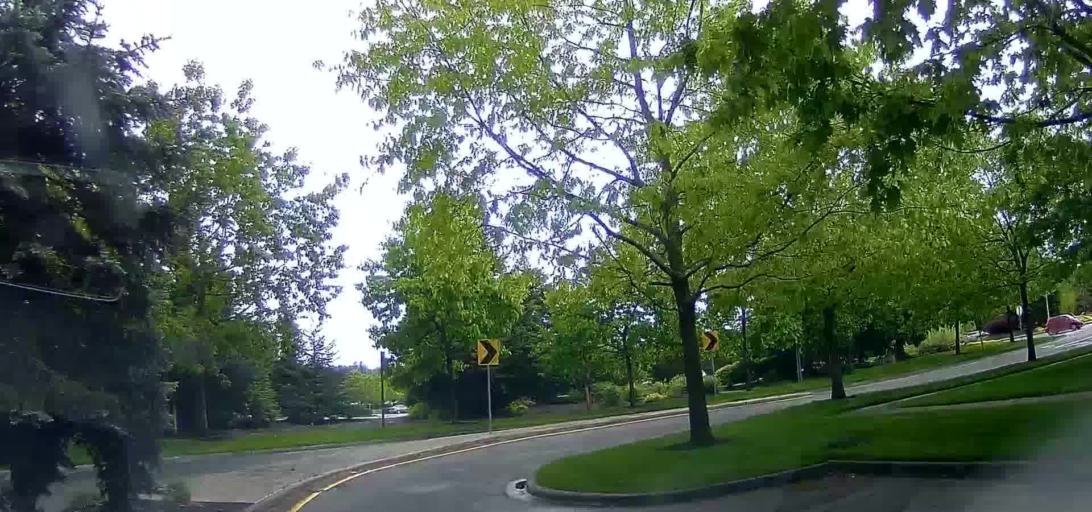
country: US
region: Washington
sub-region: Snohomish County
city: Marysville
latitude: 48.0911
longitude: -122.1898
